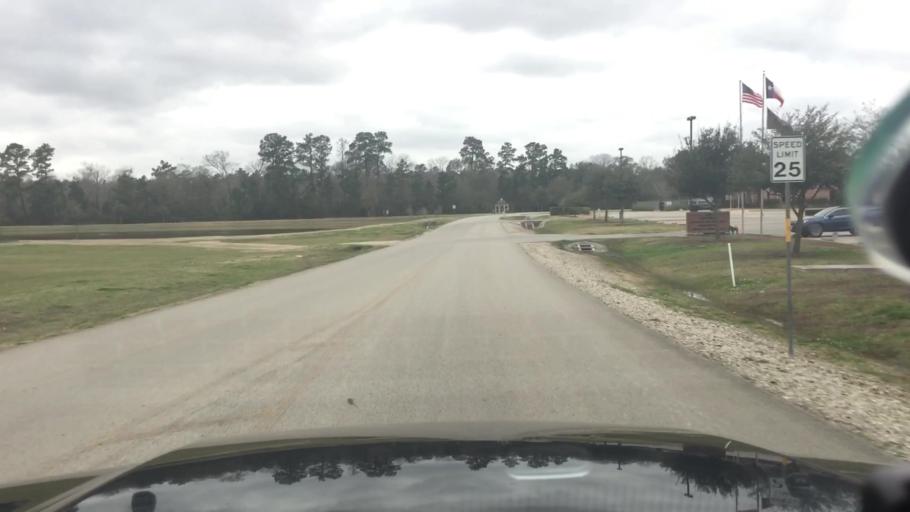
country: US
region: Texas
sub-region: Montgomery County
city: Magnolia
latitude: 30.1986
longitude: -95.7534
